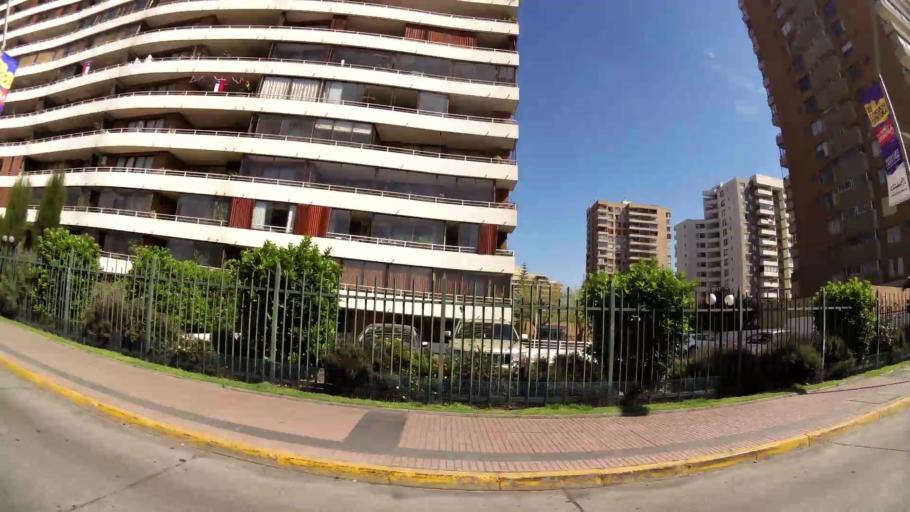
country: CL
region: Santiago Metropolitan
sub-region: Provincia de Santiago
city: Villa Presidente Frei, Nunoa, Santiago, Chile
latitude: -33.4196
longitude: -70.5531
